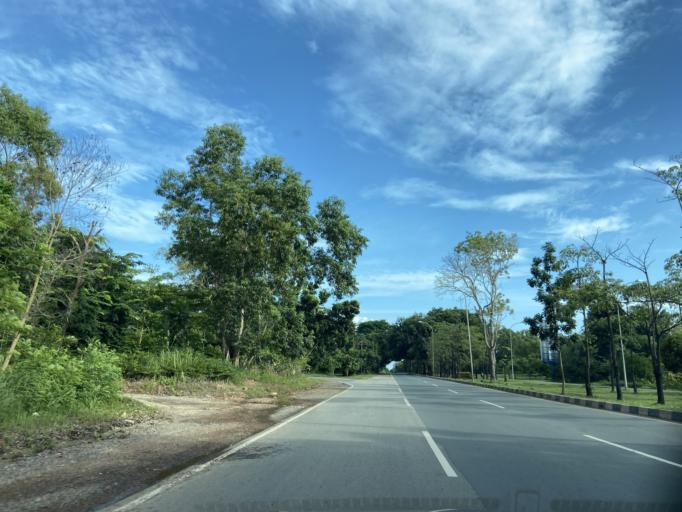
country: SG
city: Singapore
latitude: 1.1056
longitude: 104.0320
